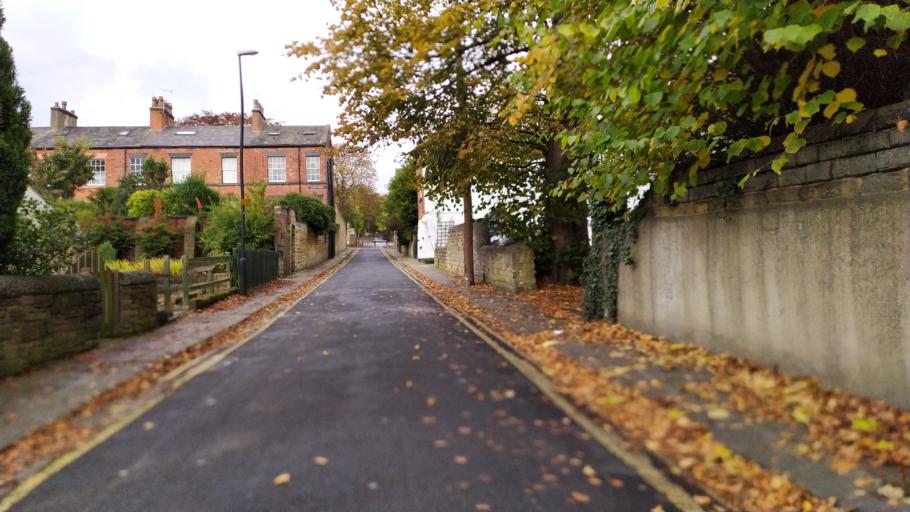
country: GB
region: England
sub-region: City and Borough of Leeds
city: Chapel Allerton
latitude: 53.8274
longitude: -1.5390
